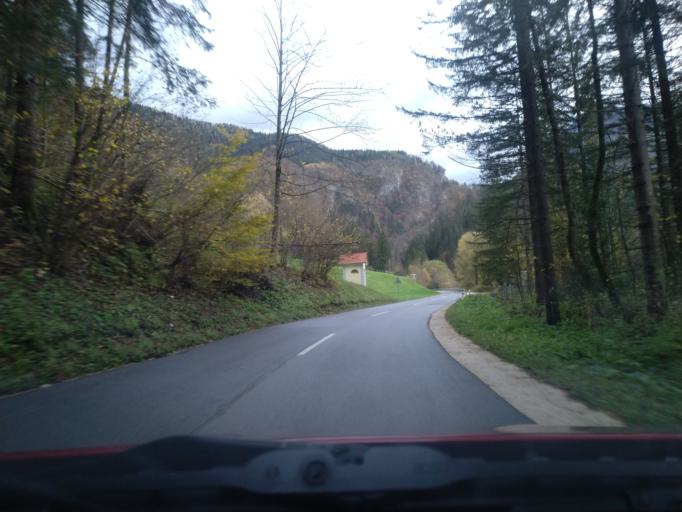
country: SI
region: Luce
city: Luce
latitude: 46.3620
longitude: 14.7348
